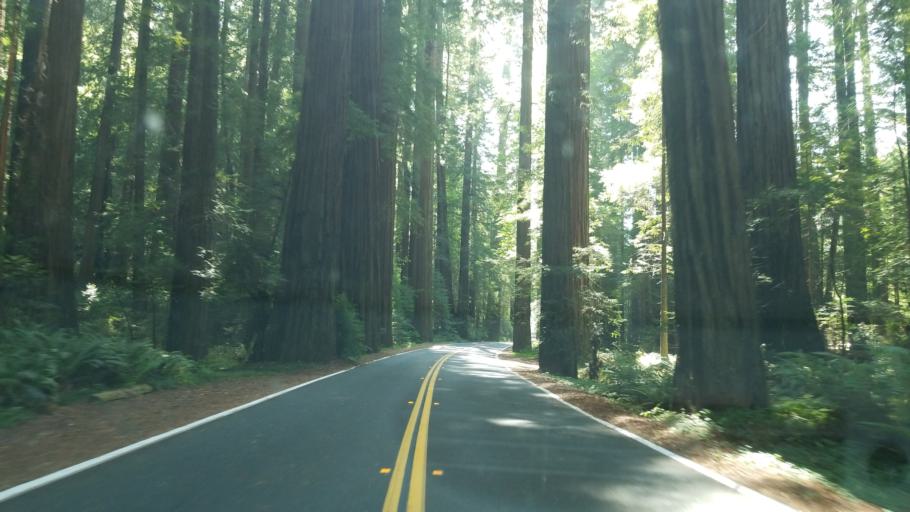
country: US
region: California
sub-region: Humboldt County
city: Rio Dell
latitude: 40.3489
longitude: -123.9286
